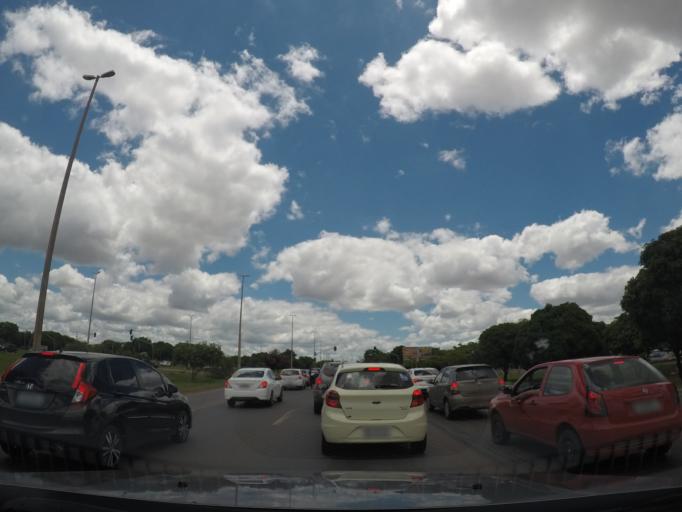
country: BR
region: Federal District
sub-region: Brasilia
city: Brasilia
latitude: -15.7777
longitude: -47.9389
